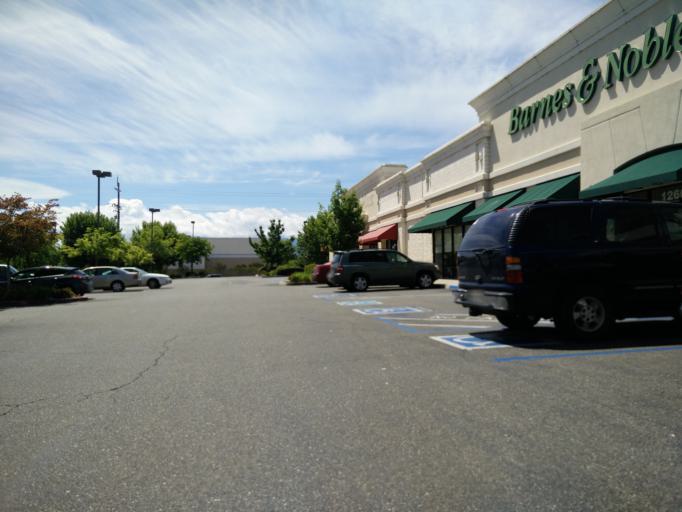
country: US
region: California
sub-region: Shasta County
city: Redding
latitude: 40.5888
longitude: -122.3520
